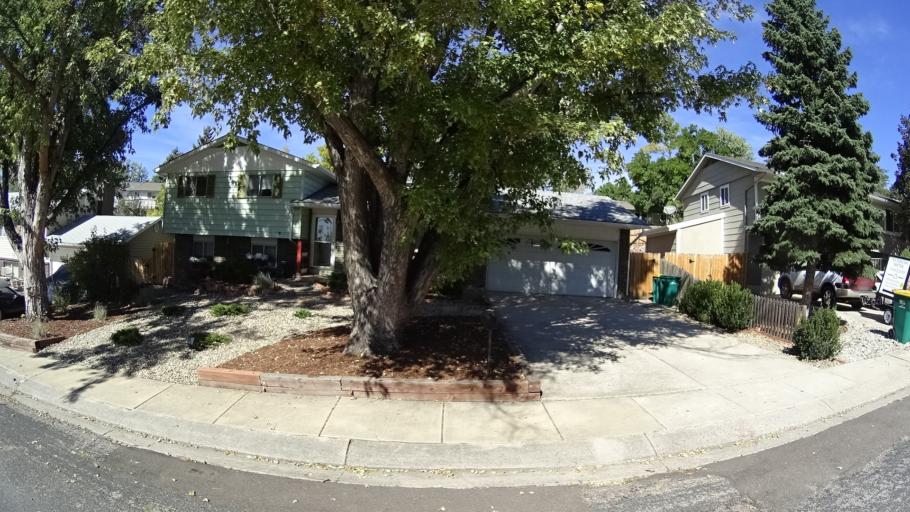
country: US
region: Colorado
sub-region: El Paso County
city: Cimarron Hills
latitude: 38.9098
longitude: -104.7713
